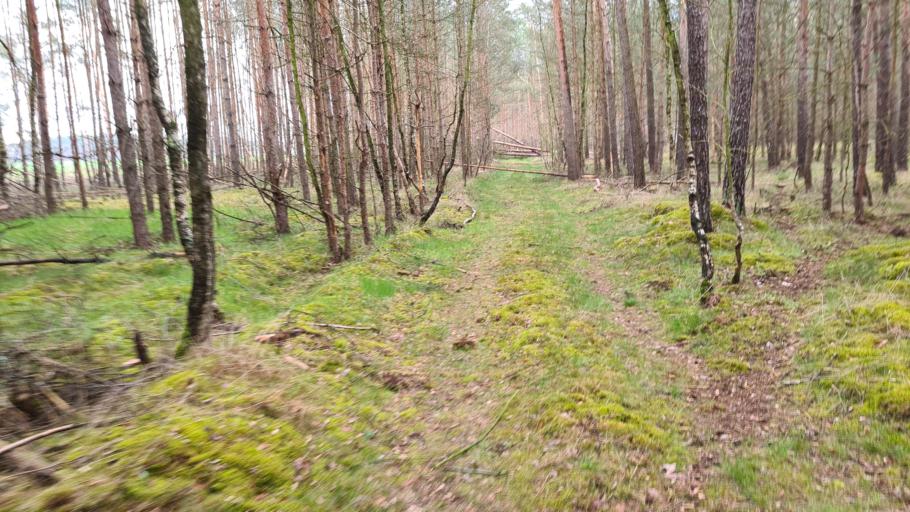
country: DE
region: Brandenburg
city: Schilda
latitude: 51.5603
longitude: 13.3845
